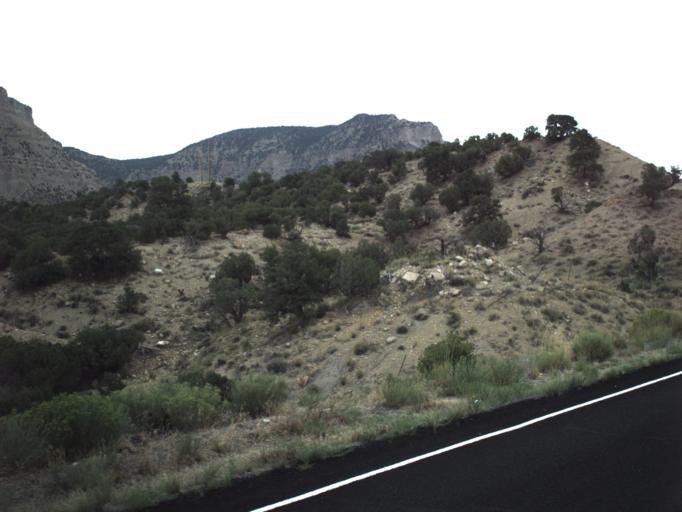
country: US
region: Utah
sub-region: Carbon County
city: East Carbon City
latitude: 39.4845
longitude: -110.4029
